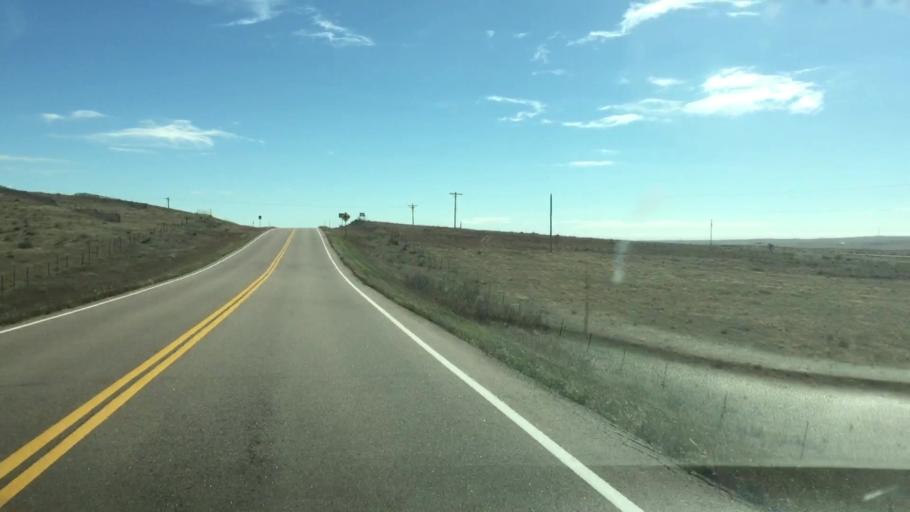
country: US
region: Colorado
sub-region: Elbert County
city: Kiowa
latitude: 39.2735
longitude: -104.1818
